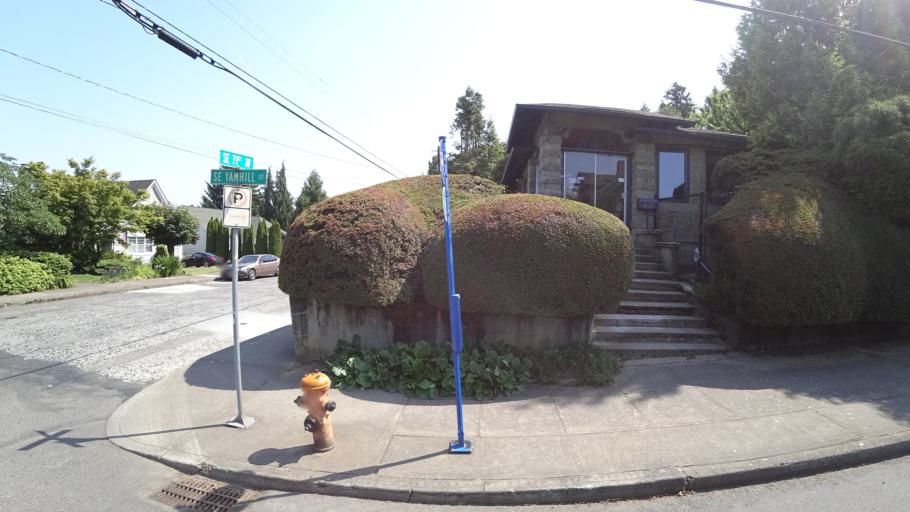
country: US
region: Oregon
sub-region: Multnomah County
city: Lents
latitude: 45.5161
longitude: -122.5899
